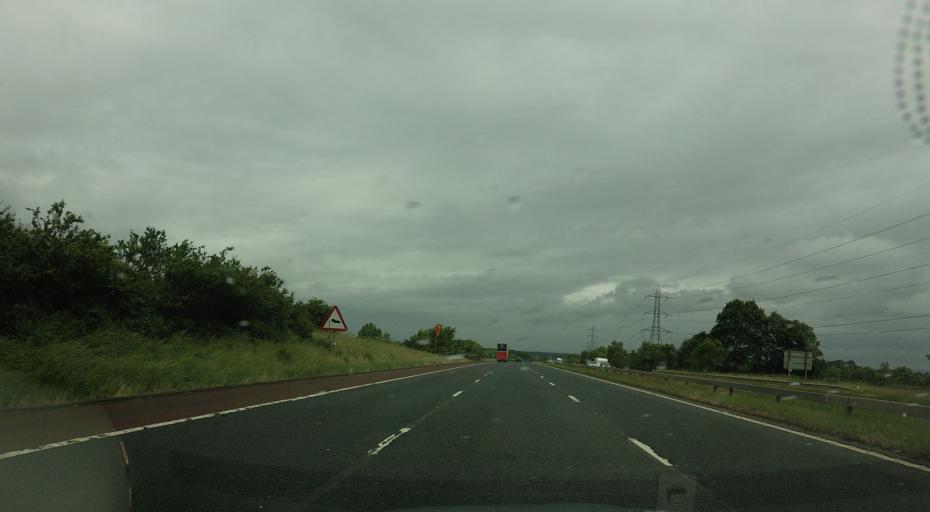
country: GB
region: England
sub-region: Cumbria
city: Scotby
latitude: 54.8848
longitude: -2.8840
